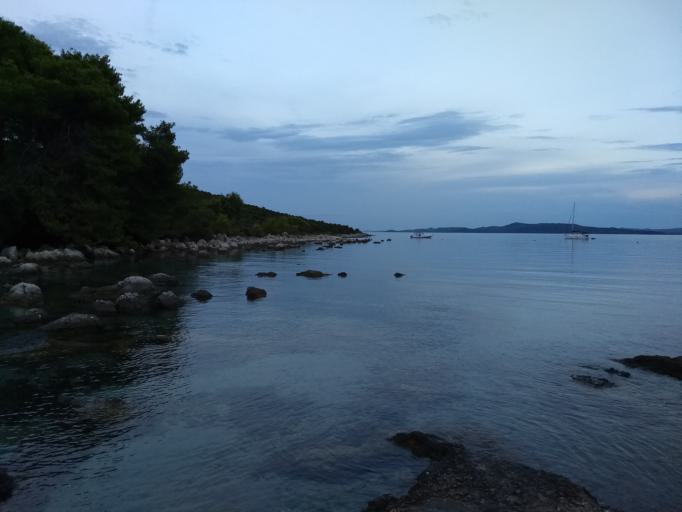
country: HR
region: Zadarska
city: Ugljan
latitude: 44.1330
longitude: 15.0699
